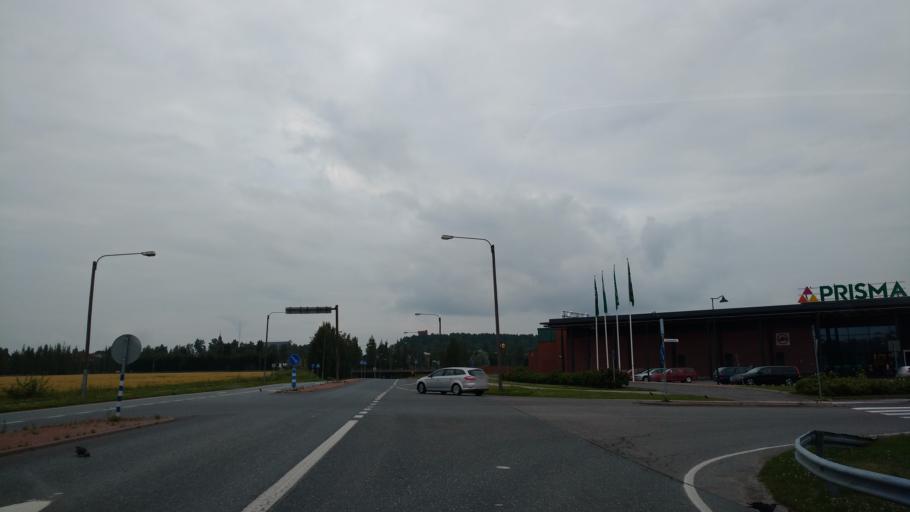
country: FI
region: Varsinais-Suomi
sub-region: Salo
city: Halikko
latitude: 60.3931
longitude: 23.0823
